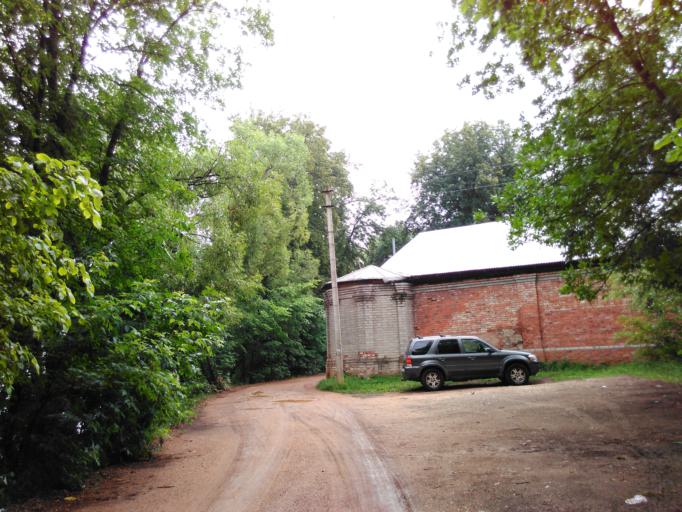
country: RU
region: Tverskaya
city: Ostashkov
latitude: 57.1682
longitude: 33.0939
